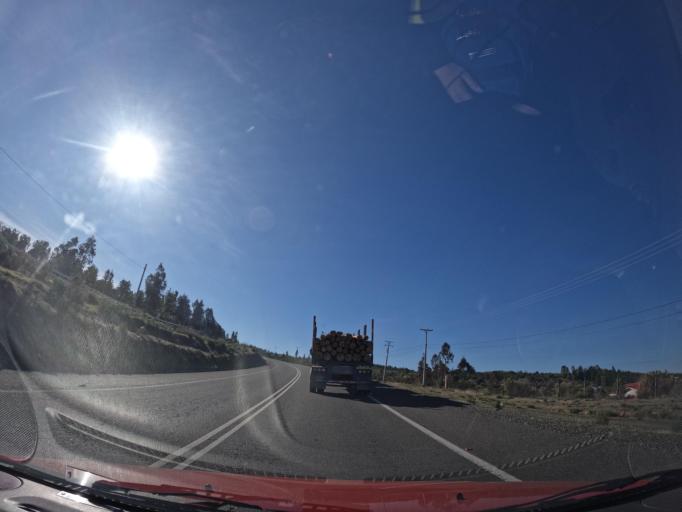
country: CL
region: Maule
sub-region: Provincia de Cauquenes
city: Cauquenes
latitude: -35.9407
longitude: -72.1966
